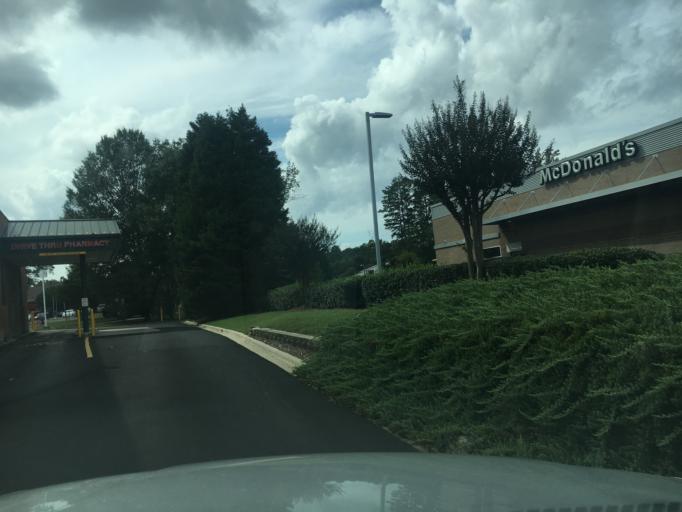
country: US
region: North Carolina
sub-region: Gaston County
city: Dallas
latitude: 35.3160
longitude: -81.1900
